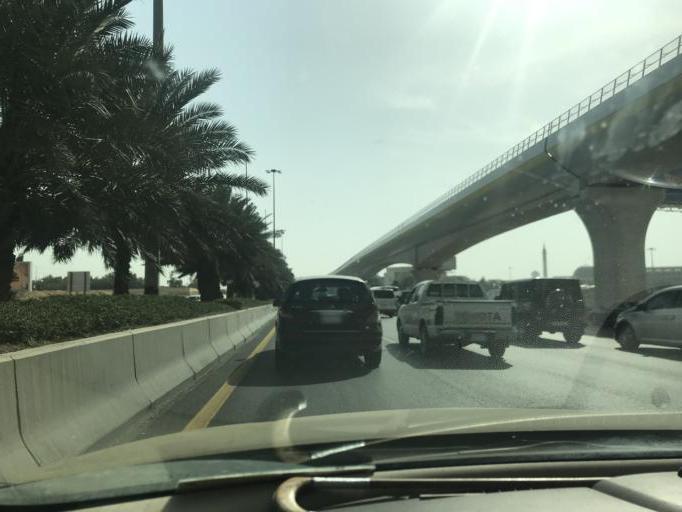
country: SA
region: Ar Riyad
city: Riyadh
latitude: 24.8192
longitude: 46.7152
